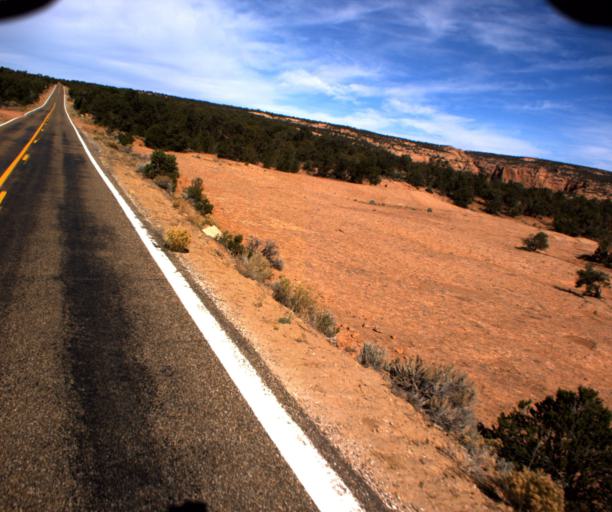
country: US
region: Arizona
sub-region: Navajo County
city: Kayenta
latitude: 36.6140
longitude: -110.5013
